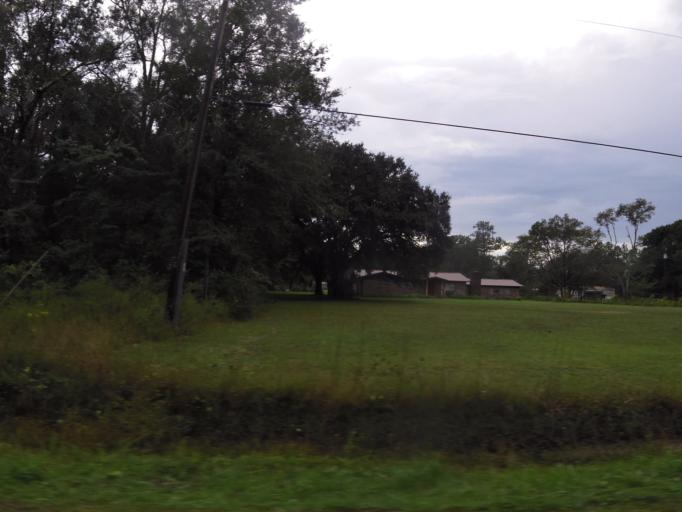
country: US
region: Florida
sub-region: Duval County
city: Baldwin
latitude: 30.3930
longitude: -81.9428
